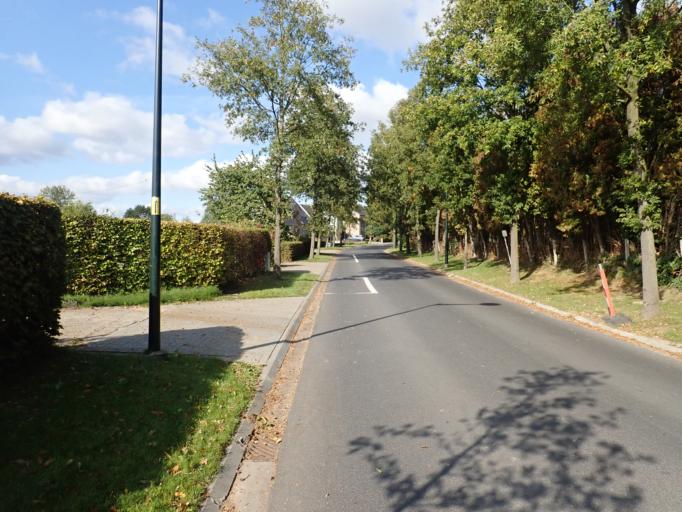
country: BE
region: Flanders
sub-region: Provincie Oost-Vlaanderen
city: Kruibeke
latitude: 51.1432
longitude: 4.2871
